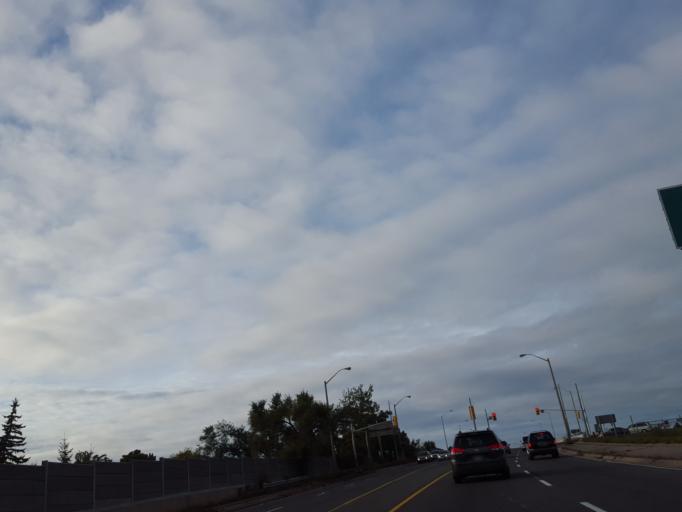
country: CA
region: Ontario
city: Scarborough
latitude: 43.7681
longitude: -79.3032
